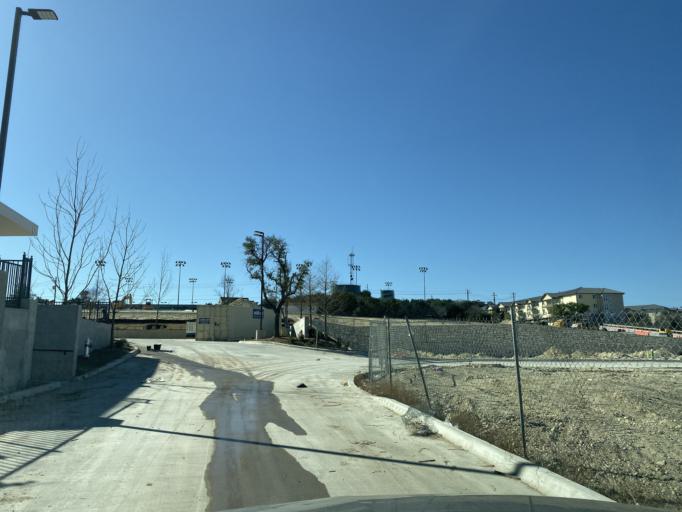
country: US
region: Texas
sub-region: Travis County
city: The Hills
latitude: 30.3302
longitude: -97.9687
